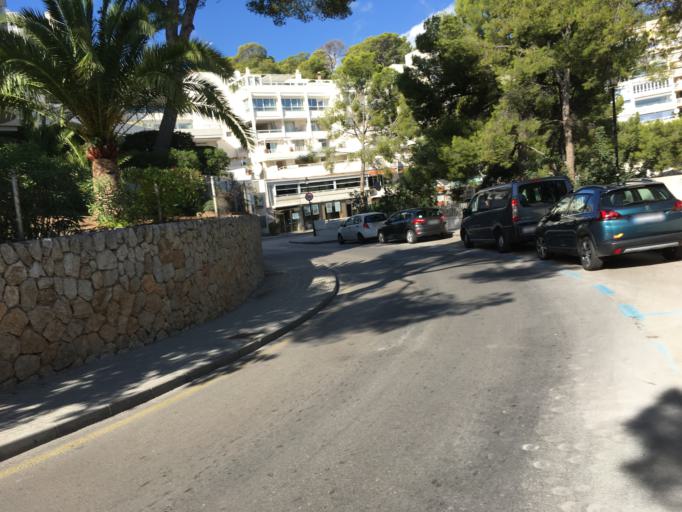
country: ES
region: Balearic Islands
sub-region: Illes Balears
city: Magaluf
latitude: 39.5362
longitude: 2.5903
